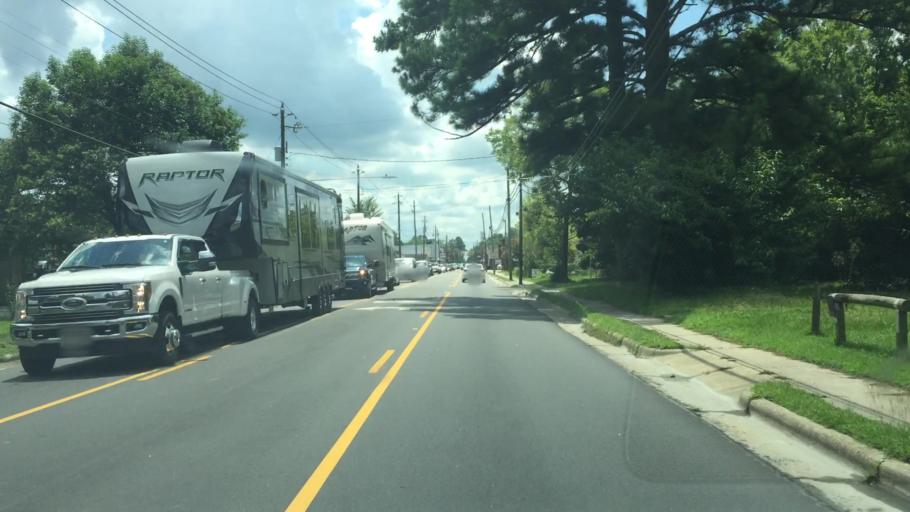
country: US
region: North Carolina
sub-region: Columbus County
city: Chadbourn
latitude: 34.3269
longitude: -78.8265
